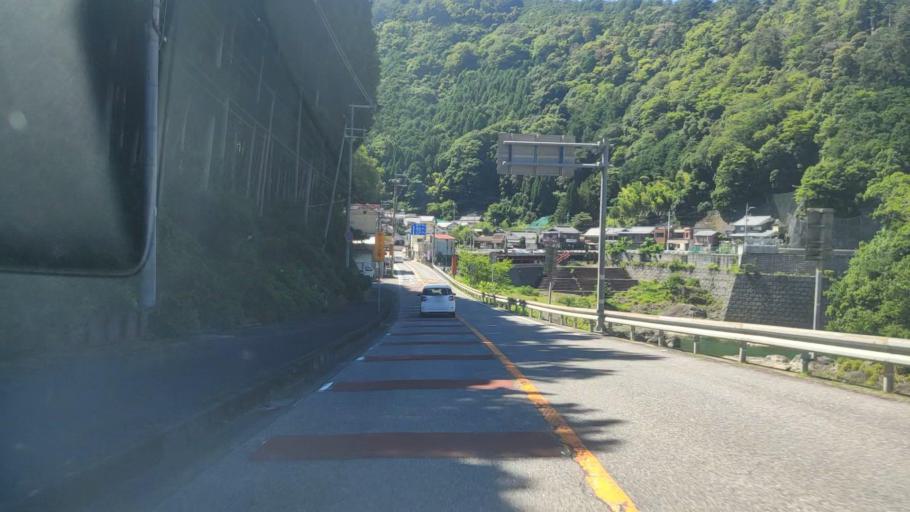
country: JP
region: Nara
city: Yoshino-cho
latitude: 34.3553
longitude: 135.9253
